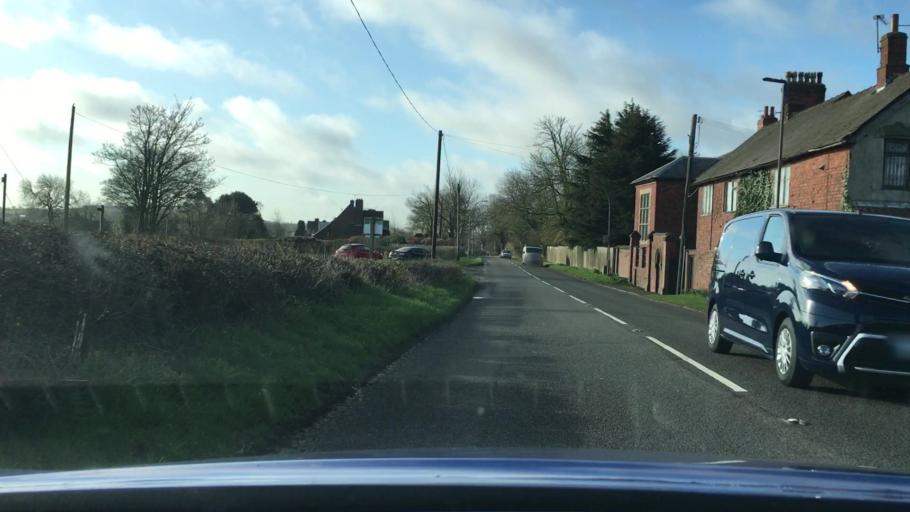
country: GB
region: England
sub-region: Derbyshire
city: Tibshelf
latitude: 53.1542
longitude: -1.3380
